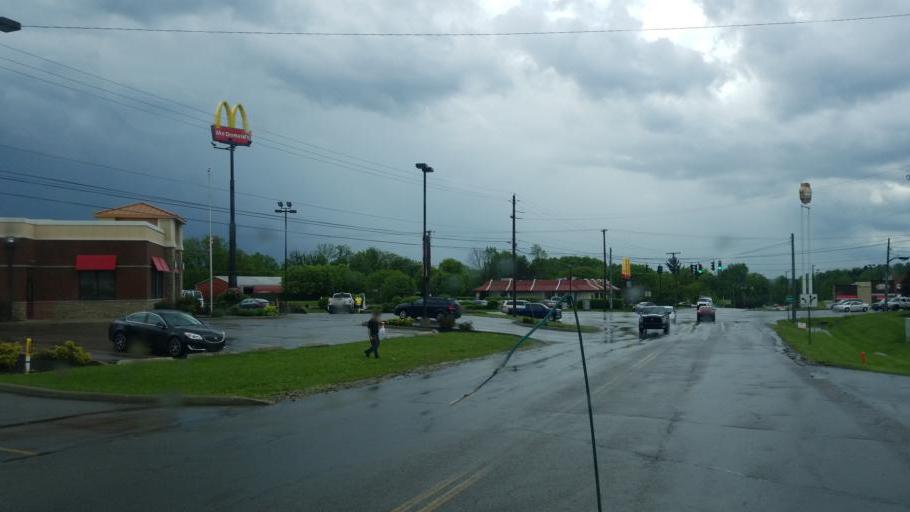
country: US
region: Ohio
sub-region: Richland County
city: Lincoln Heights
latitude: 40.7777
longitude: -82.4750
